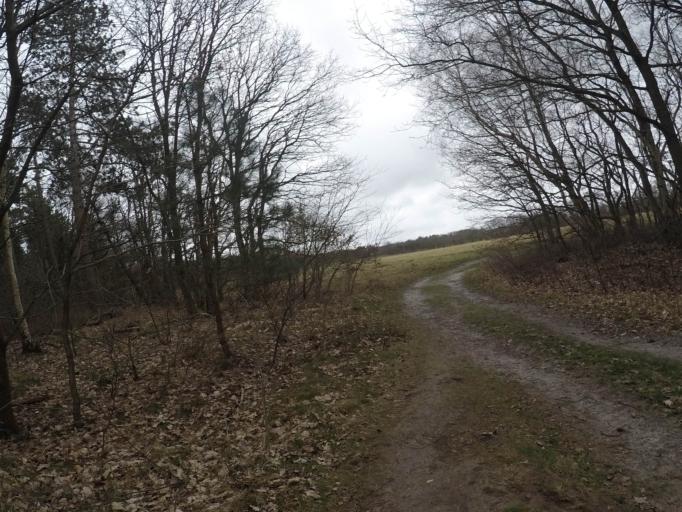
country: DE
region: Lower Saxony
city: Nordholz
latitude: 53.8218
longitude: 8.5991
